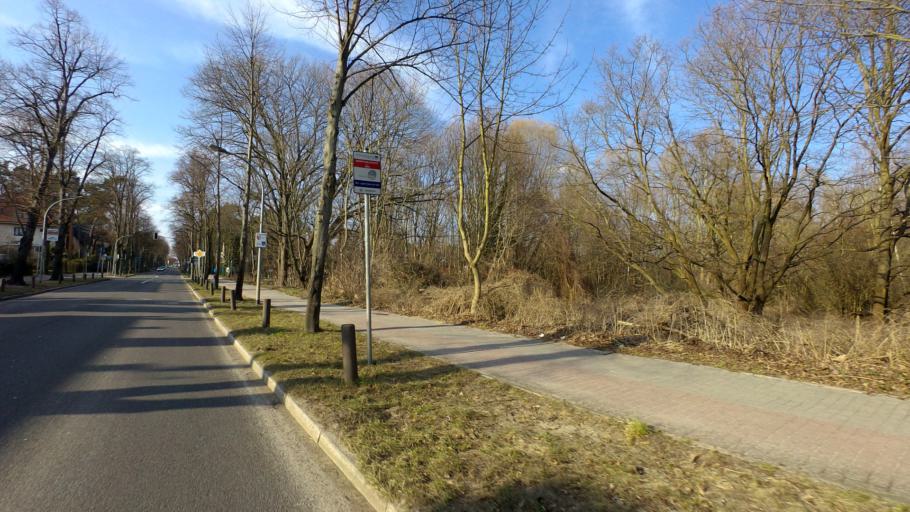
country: DE
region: Brandenburg
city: Kleinmachnow
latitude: 52.4024
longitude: 13.2384
